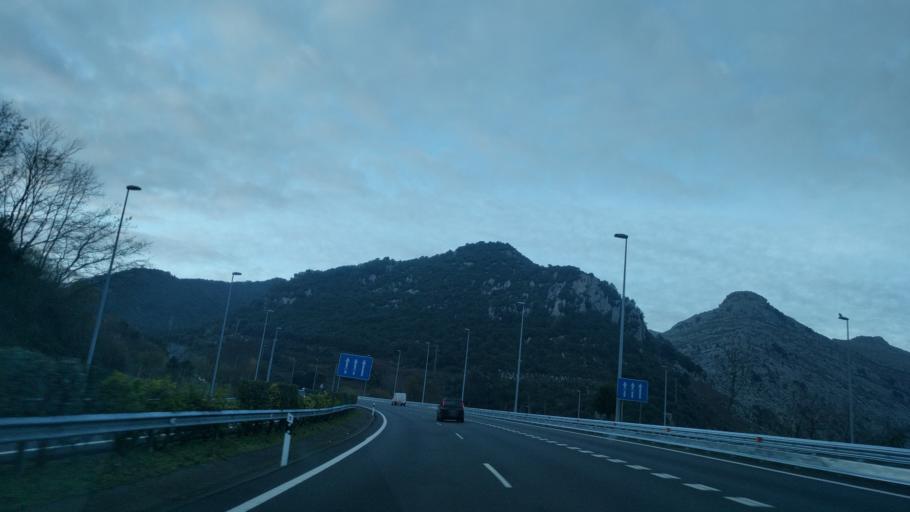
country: ES
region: Cantabria
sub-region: Provincia de Cantabria
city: Liendo
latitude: 43.3891
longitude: -3.3295
